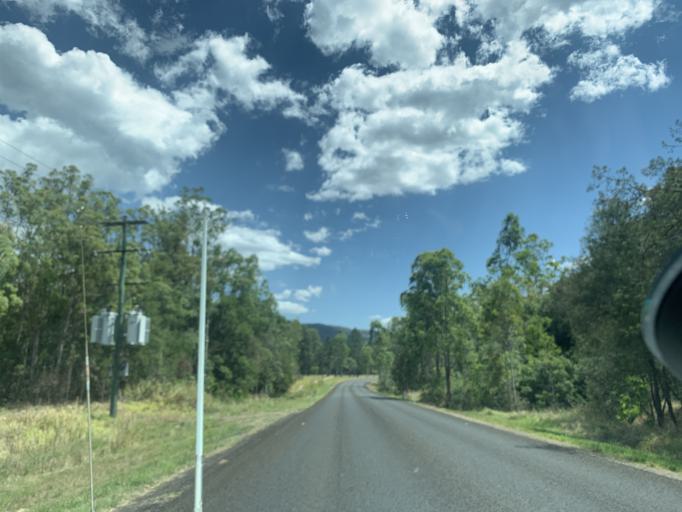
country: AU
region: Queensland
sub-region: Tablelands
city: Atherton
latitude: -17.3161
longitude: 145.4503
